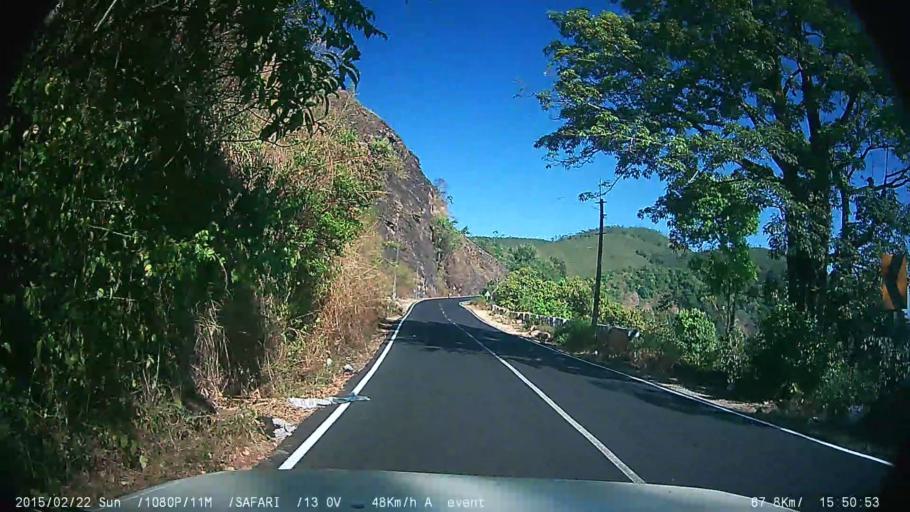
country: IN
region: Kerala
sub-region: Kottayam
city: Erattupetta
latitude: 9.5687
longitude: 77.0054
